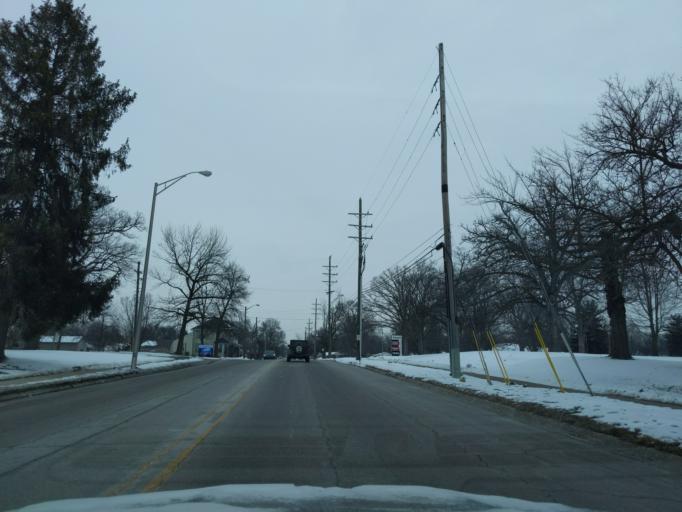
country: US
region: Indiana
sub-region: Tippecanoe County
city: Lafayette
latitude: 40.4004
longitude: -86.8767
